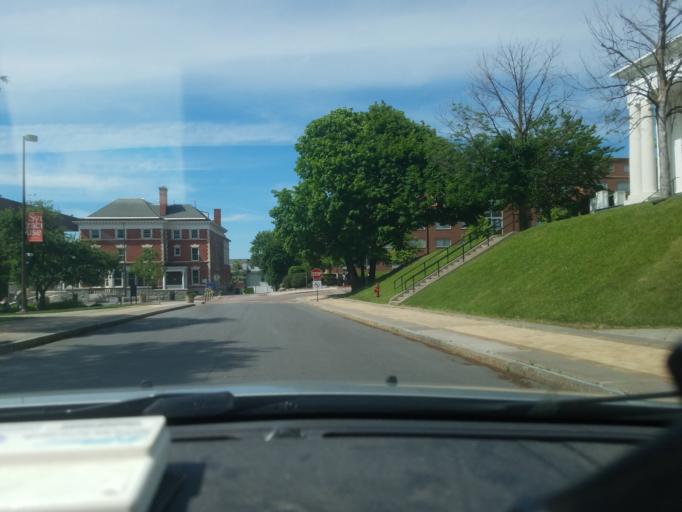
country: US
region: New York
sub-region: Onondaga County
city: Syracuse
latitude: 43.0389
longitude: -76.1316
